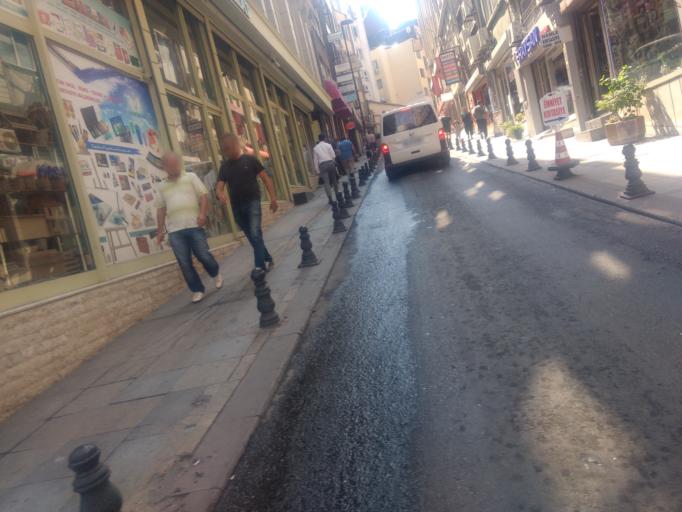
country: TR
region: Istanbul
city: Eminoenue
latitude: 41.0130
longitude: 28.9751
